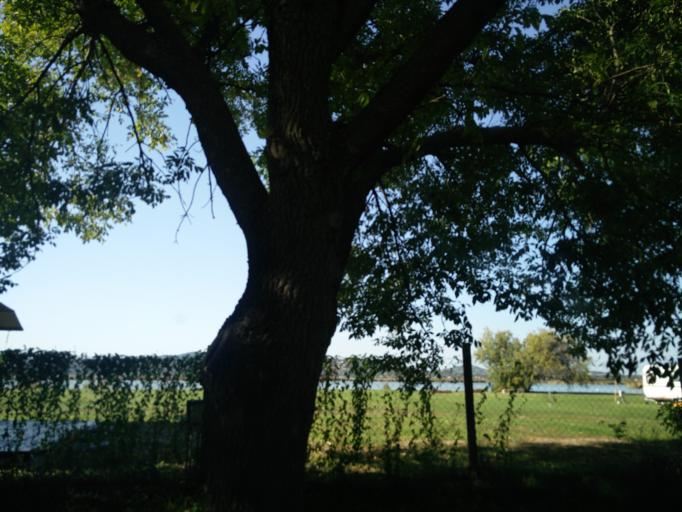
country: HU
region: Fejer
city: Gardony
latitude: 47.2185
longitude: 18.6442
